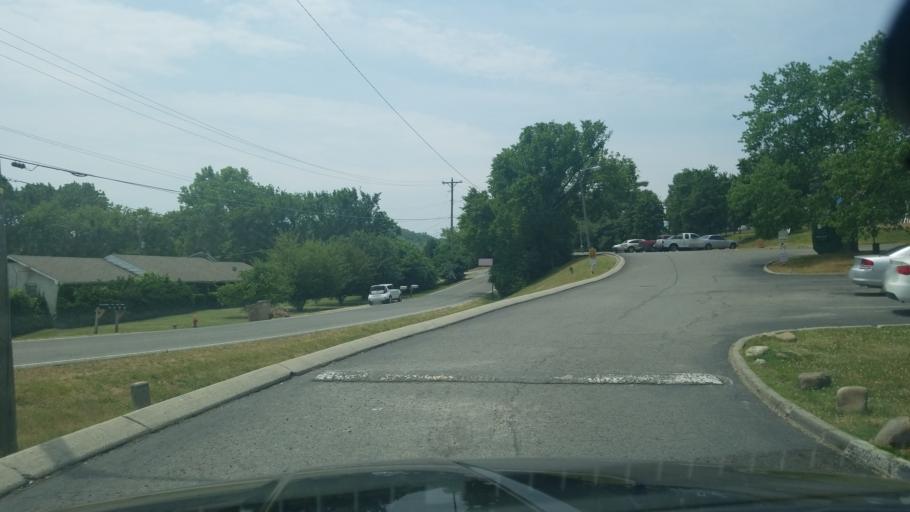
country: US
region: Tennessee
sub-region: Davidson County
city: Goodlettsville
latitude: 36.2504
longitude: -86.7427
